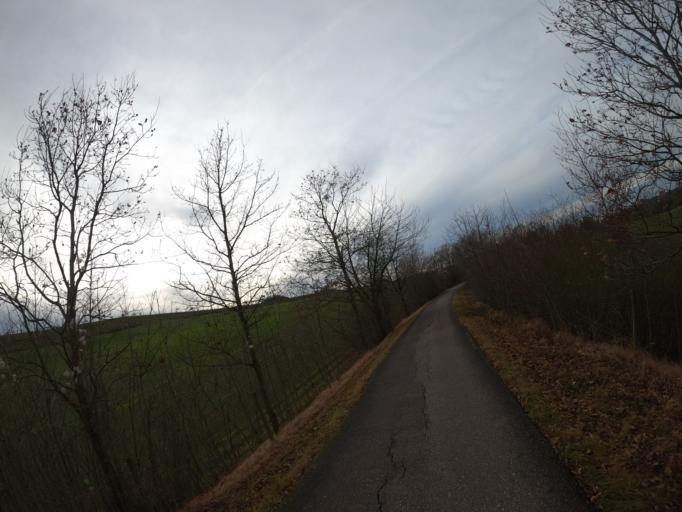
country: DE
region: Baden-Wuerttemberg
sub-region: Regierungsbezirk Stuttgart
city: Ottenbach
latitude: 48.7564
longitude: 9.7364
